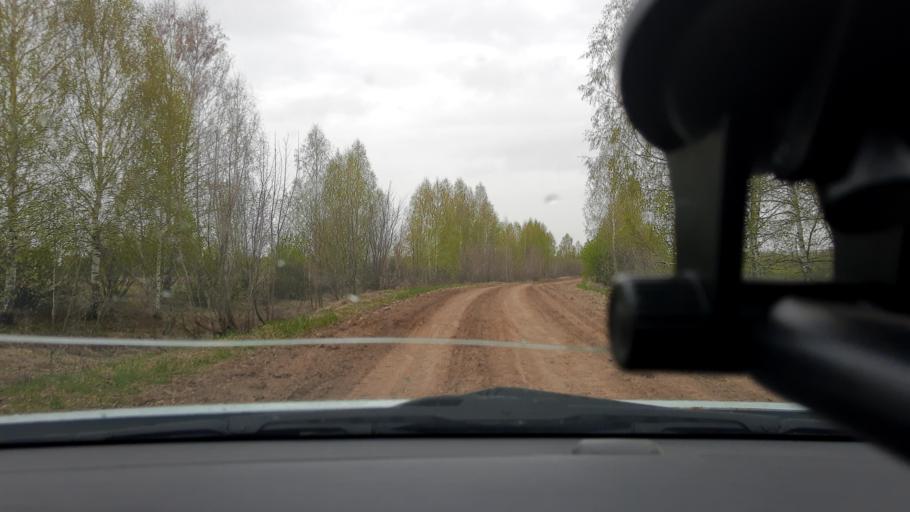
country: RU
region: Bashkortostan
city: Pavlovka
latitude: 55.4284
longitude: 56.3469
